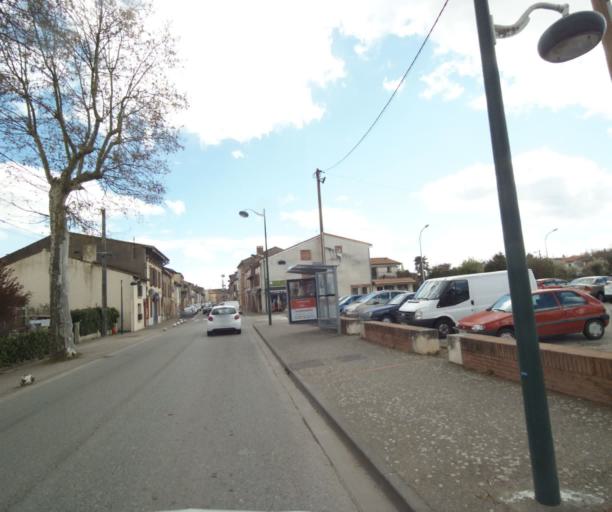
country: FR
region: Midi-Pyrenees
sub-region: Departement de l'Ariege
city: Saverdun
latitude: 43.2376
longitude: 1.5739
